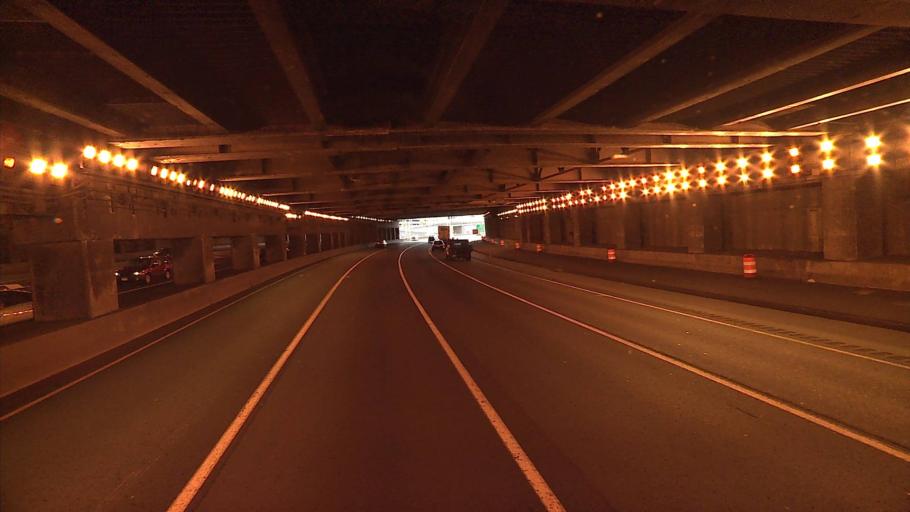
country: US
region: Connecticut
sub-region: Hartford County
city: Hartford
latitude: 41.7698
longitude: -72.6741
